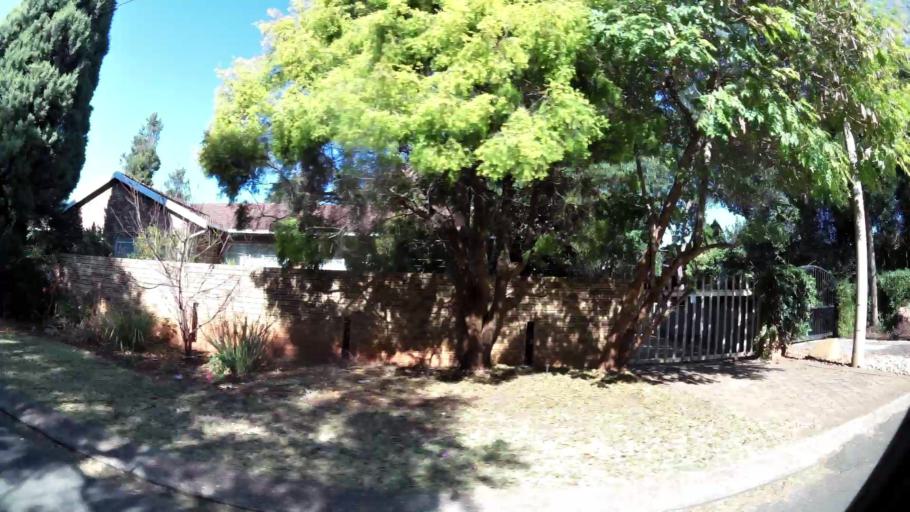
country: ZA
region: Gauteng
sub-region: City of Johannesburg Metropolitan Municipality
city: Roodepoort
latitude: -26.1192
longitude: 27.8593
